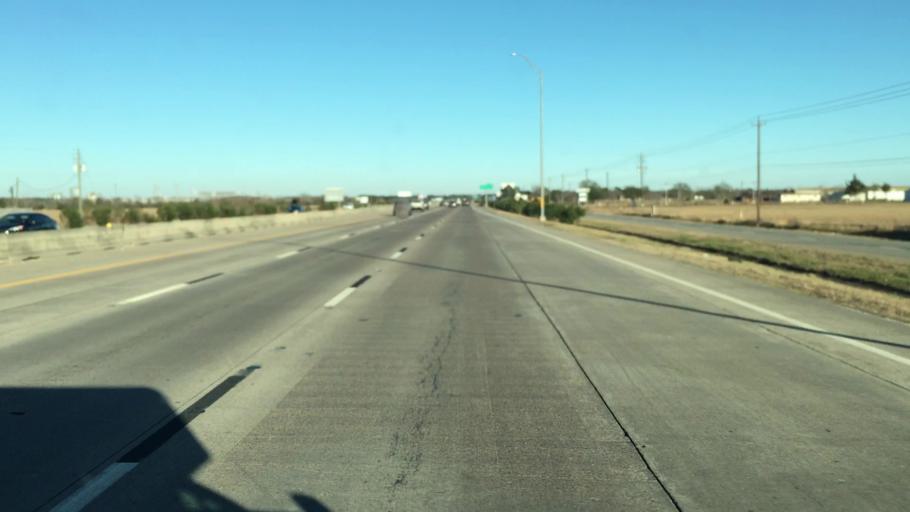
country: US
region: Texas
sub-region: Harris County
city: Baytown
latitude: 29.8090
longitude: -94.9581
